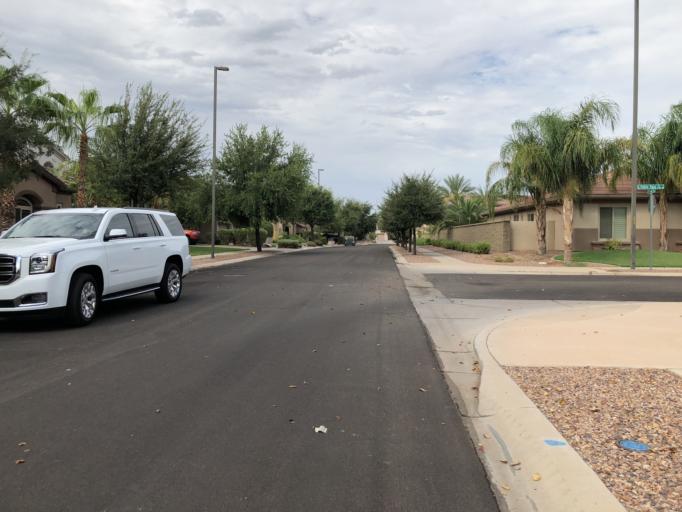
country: US
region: Arizona
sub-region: Maricopa County
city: Queen Creek
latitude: 33.2656
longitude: -111.6925
